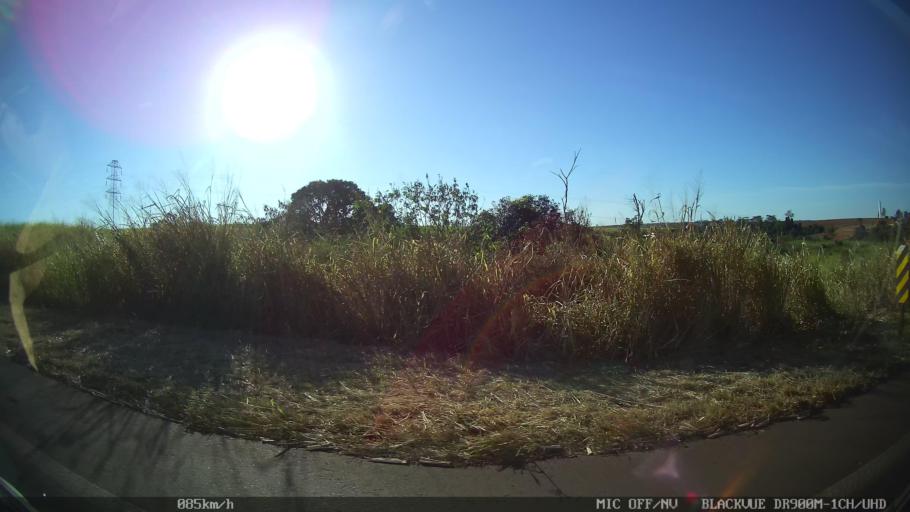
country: BR
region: Sao Paulo
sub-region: Olimpia
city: Olimpia
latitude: -20.6948
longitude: -48.9265
